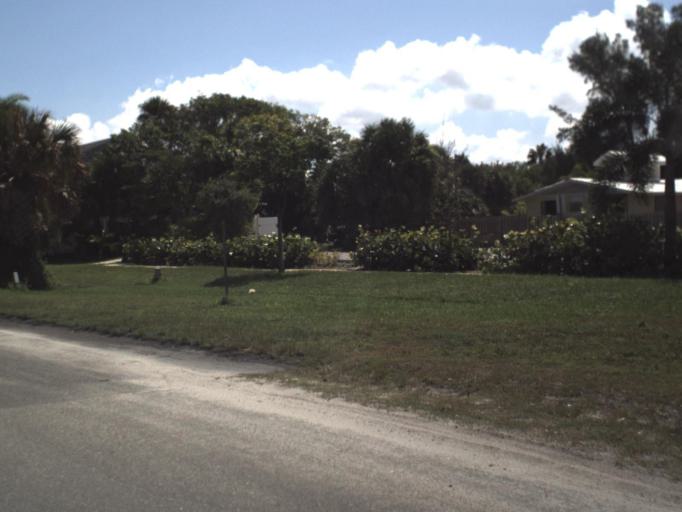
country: US
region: Florida
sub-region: Manatee County
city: Holmes Beach
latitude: 27.4971
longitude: -82.7108
